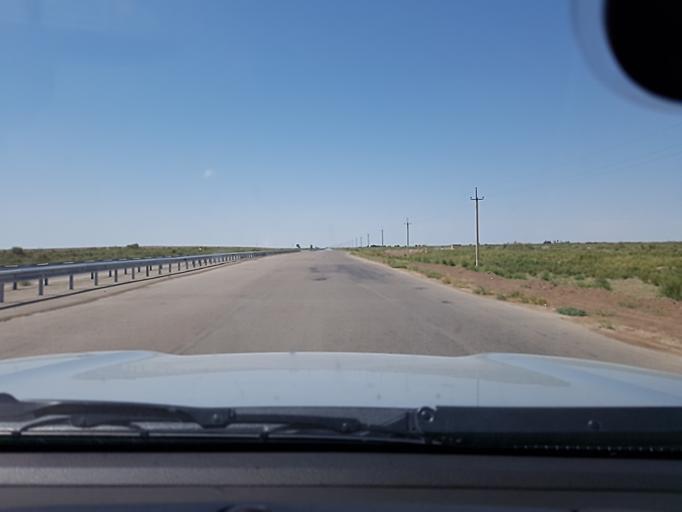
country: TM
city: Akdepe
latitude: 41.7402
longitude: 59.2106
